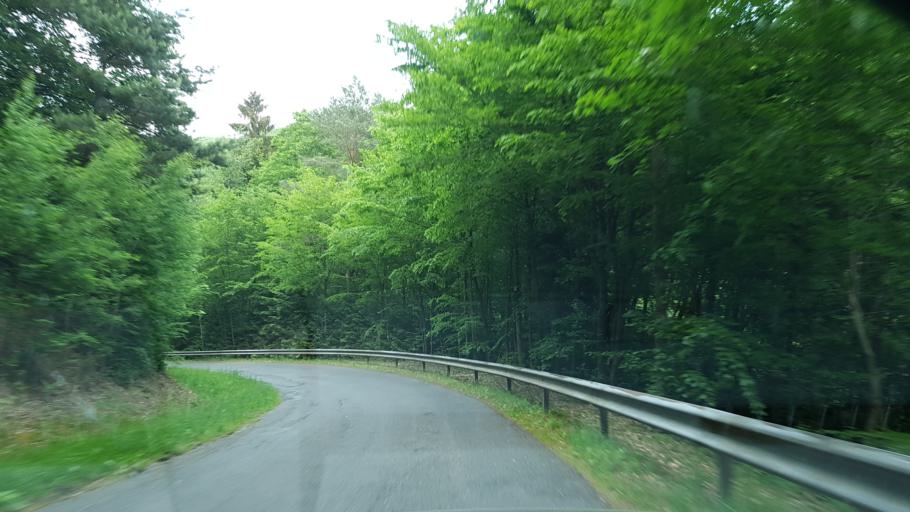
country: DE
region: North Rhine-Westphalia
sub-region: Regierungsbezirk Koln
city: Eitorf
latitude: 50.7814
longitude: 7.4188
